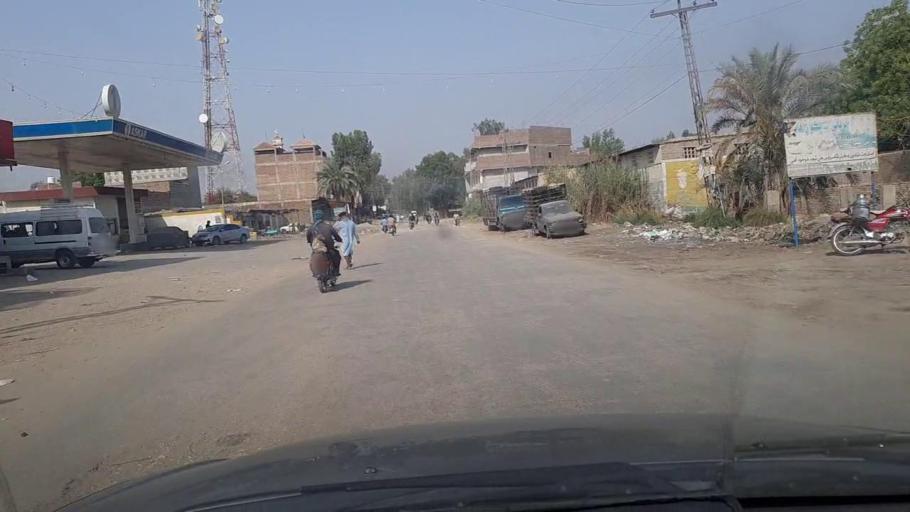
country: PK
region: Sindh
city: Mirpur Mathelo
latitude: 28.0254
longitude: 69.5676
